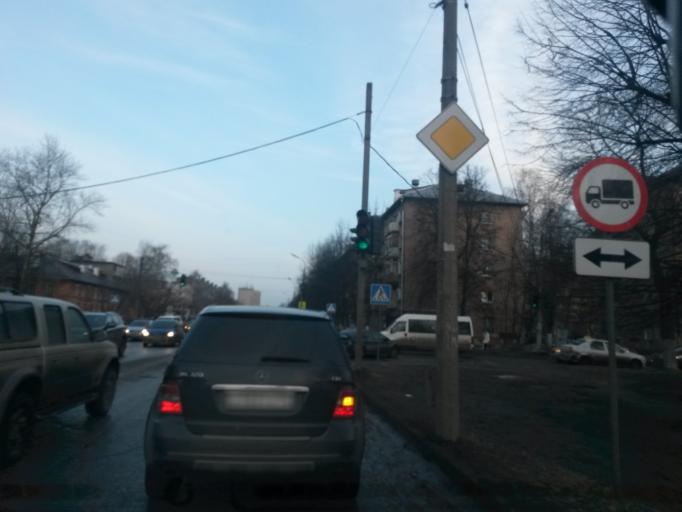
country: RU
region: Jaroslavl
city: Yaroslavl
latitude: 57.6306
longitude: 39.8403
